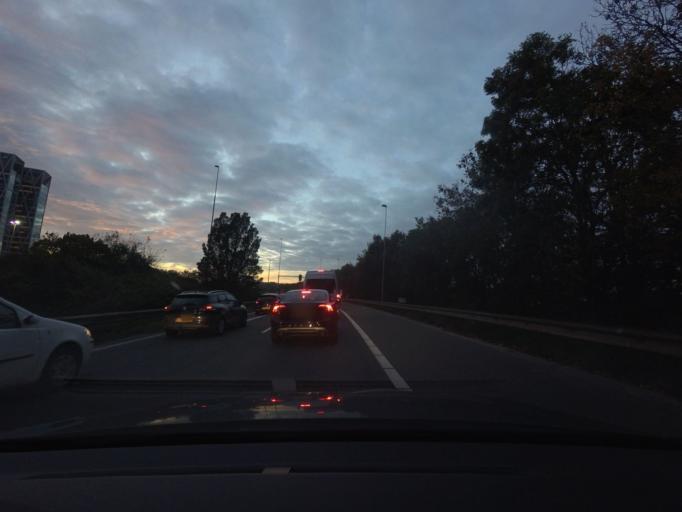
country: NL
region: North Holland
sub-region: Gemeente Amsterdam
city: Amsterdam
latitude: 52.3387
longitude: 4.8887
